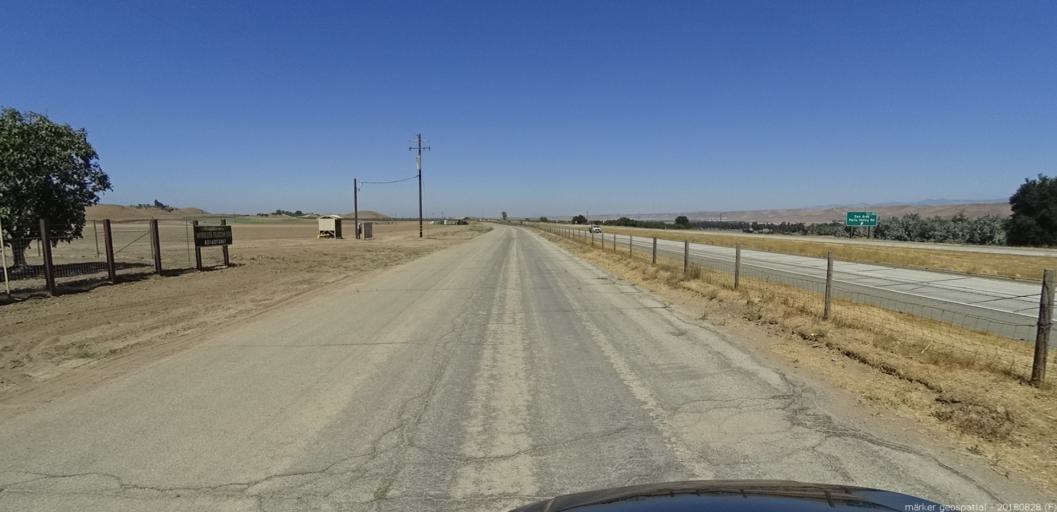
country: US
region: California
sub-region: San Luis Obispo County
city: Lake Nacimiento
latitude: 36.0071
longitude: -120.9185
